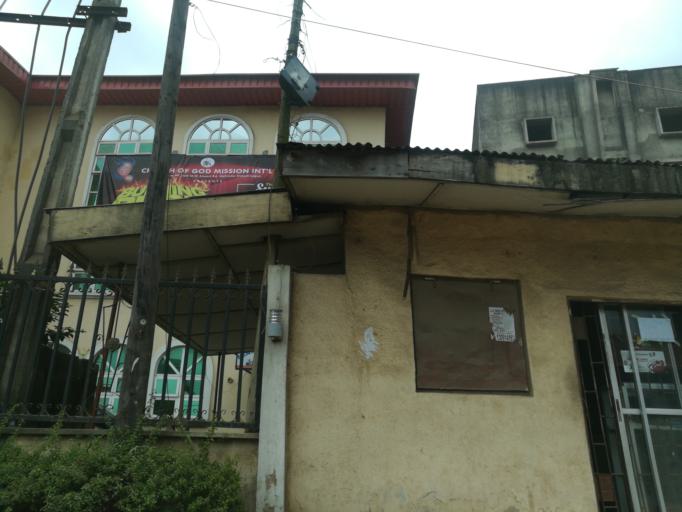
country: NG
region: Lagos
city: Oshodi
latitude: 6.5535
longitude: 3.3286
